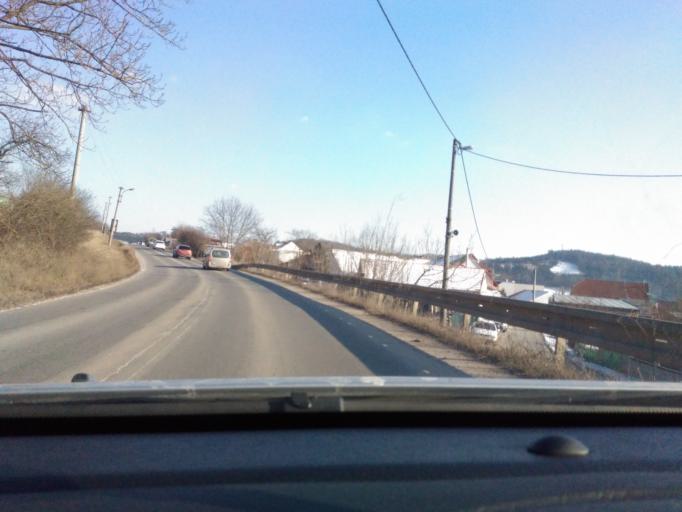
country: CZ
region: South Moravian
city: Cebin
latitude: 49.3133
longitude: 16.4805
